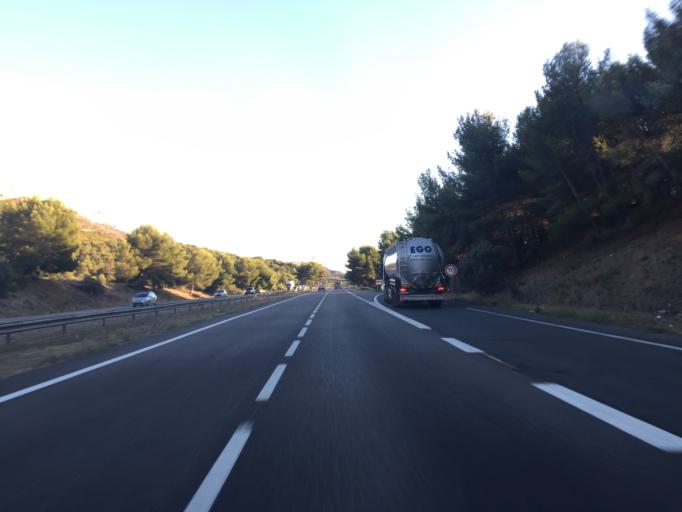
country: FR
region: Provence-Alpes-Cote d'Azur
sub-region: Departement des Bouches-du-Rhone
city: Rognac
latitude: 43.4977
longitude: 5.2389
